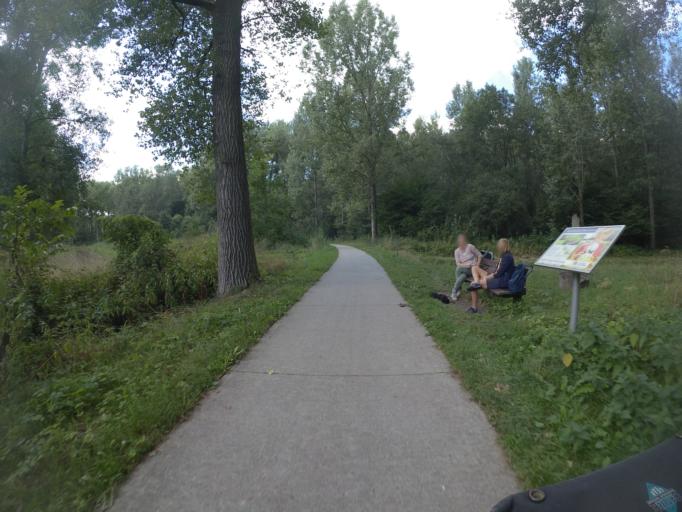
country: NL
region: North Brabant
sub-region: Gemeente Schijndel
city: Schijndel
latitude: 51.6352
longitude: 5.4650
